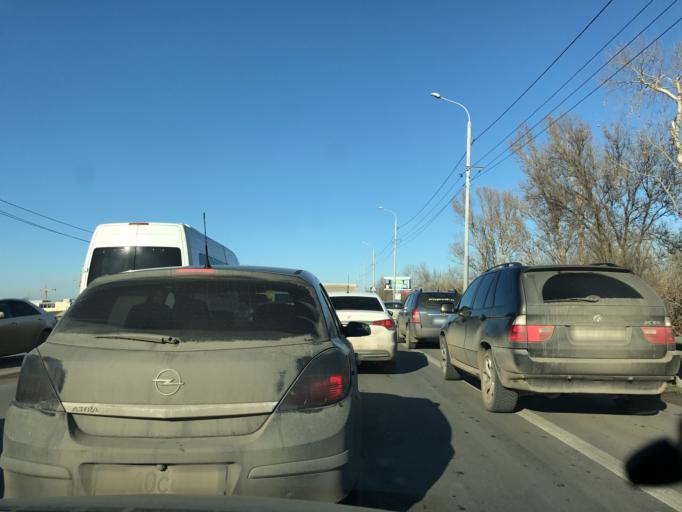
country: RU
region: Rostov
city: Rostov-na-Donu
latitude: 47.1976
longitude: 39.7308
